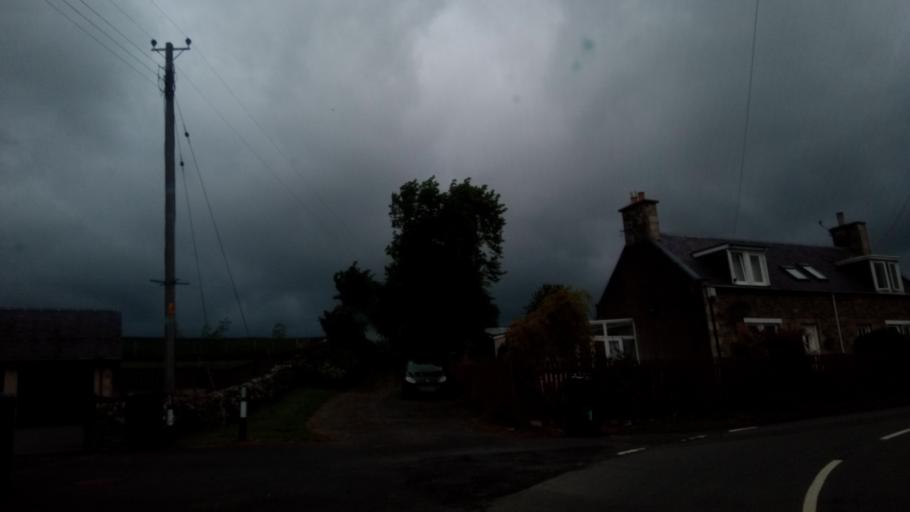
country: GB
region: Scotland
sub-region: The Scottish Borders
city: Hawick
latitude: 55.4570
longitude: -2.7534
